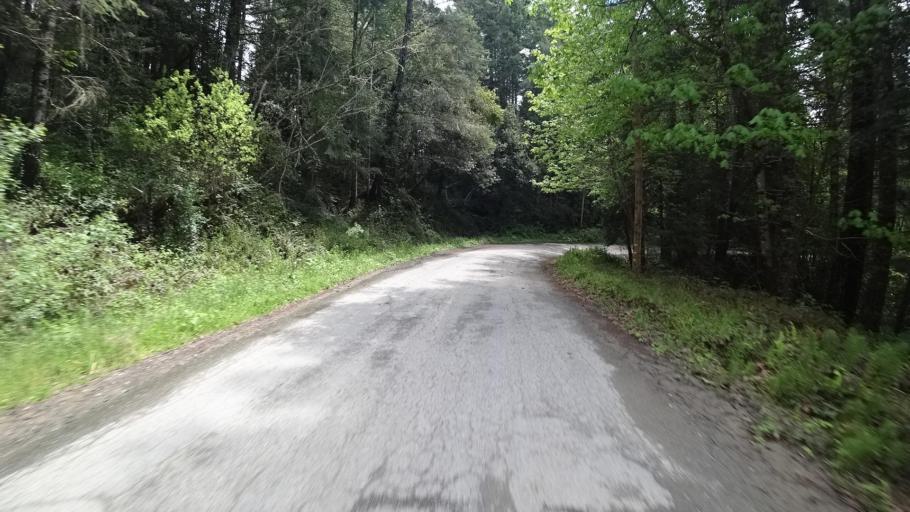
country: US
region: California
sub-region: Humboldt County
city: Blue Lake
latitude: 40.7945
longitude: -123.8764
